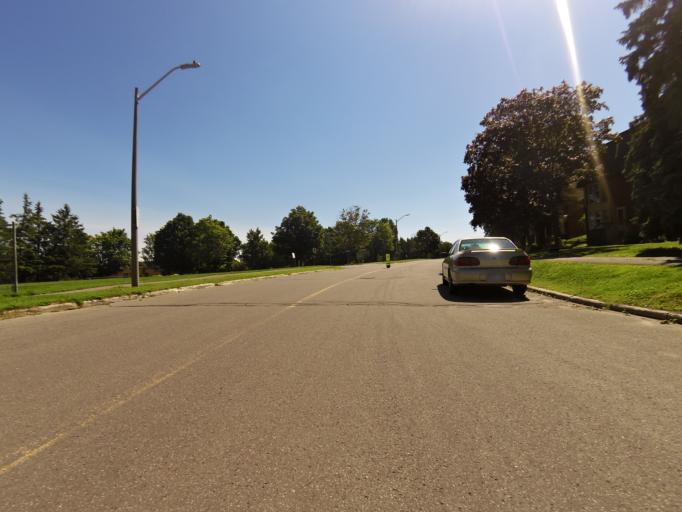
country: CA
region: Ontario
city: Ottawa
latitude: 45.3548
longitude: -75.6672
